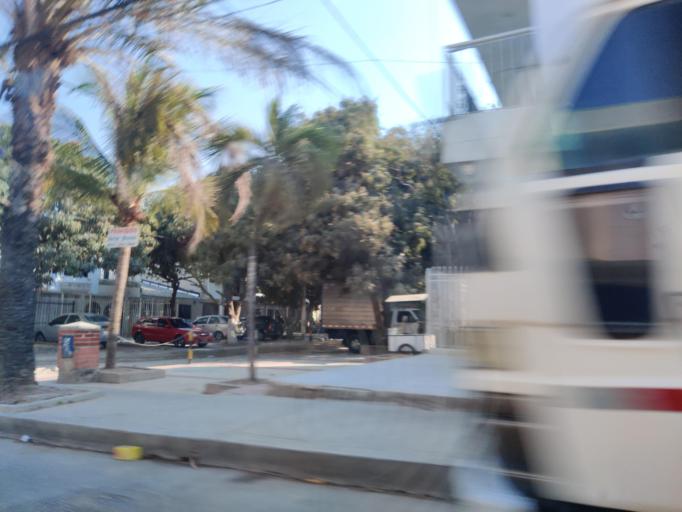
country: CO
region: Atlantico
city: Soledad
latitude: 10.9108
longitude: -74.8007
